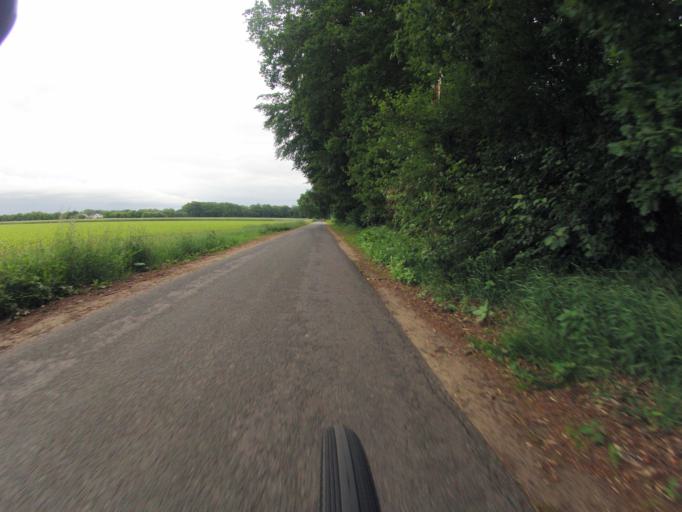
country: DE
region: North Rhine-Westphalia
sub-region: Regierungsbezirk Munster
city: Saerbeck
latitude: 52.1717
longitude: 7.6095
